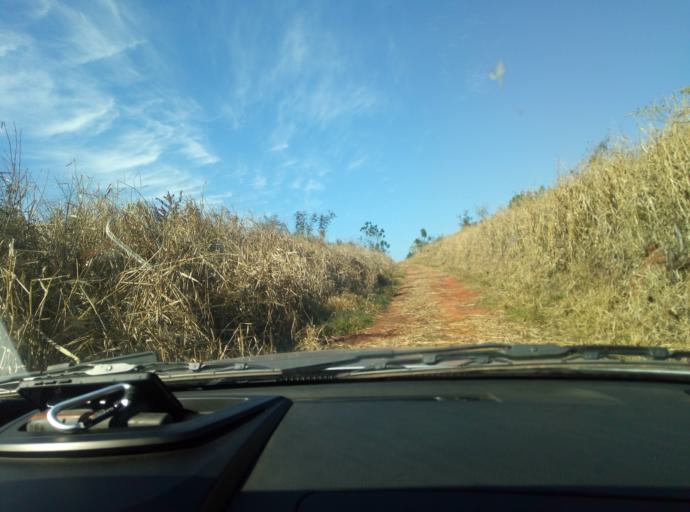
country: PY
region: Caaguazu
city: Carayao
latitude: -25.1754
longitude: -56.3085
